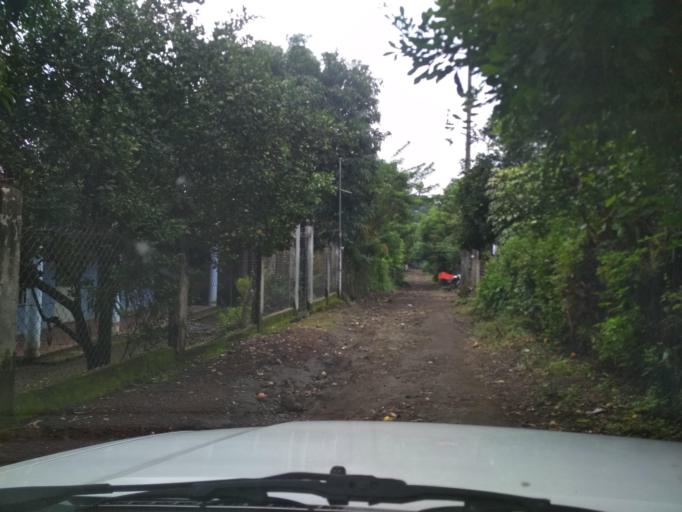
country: MX
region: Veracruz
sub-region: San Andres Tuxtla
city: Matacapan
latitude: 18.4332
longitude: -95.1714
